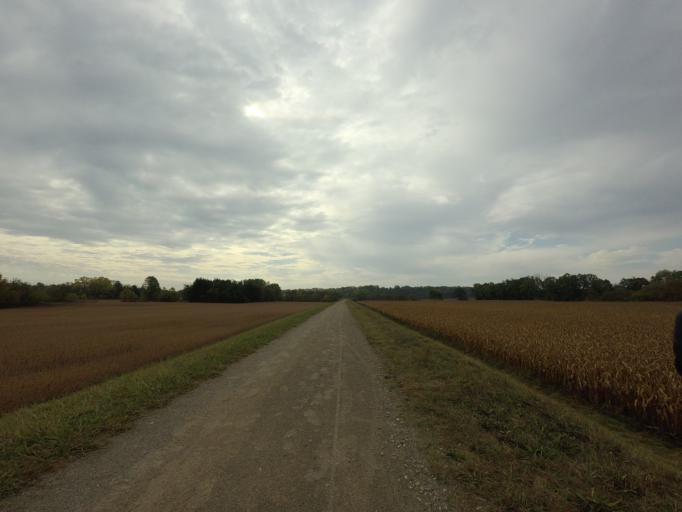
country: CA
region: Ontario
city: Brantford
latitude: 43.1191
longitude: -80.2558
